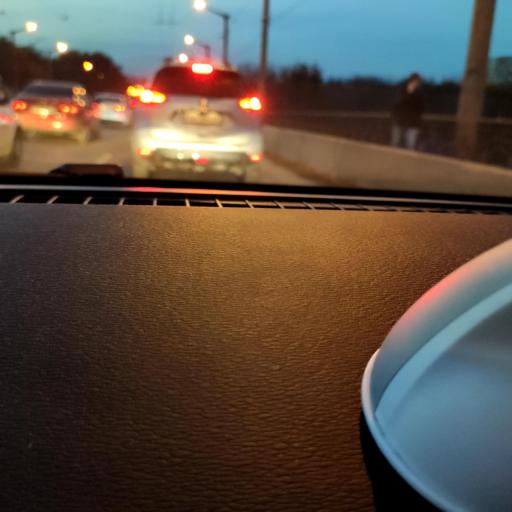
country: RU
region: Samara
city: Samara
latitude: 53.2017
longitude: 50.2415
